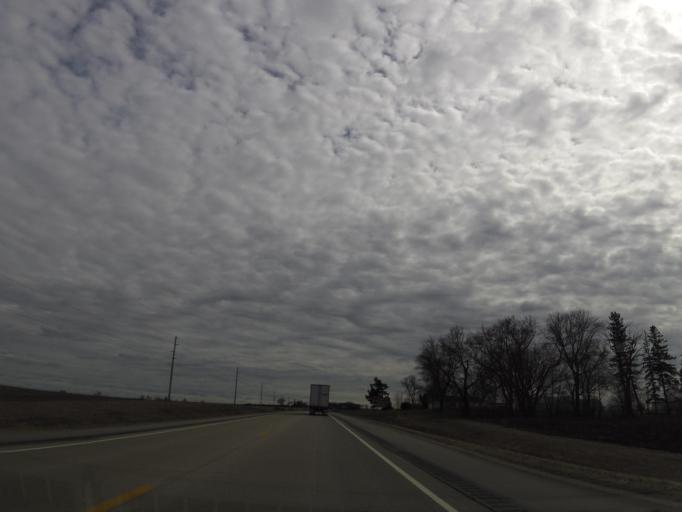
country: US
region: Minnesota
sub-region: Fillmore County
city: Spring Valley
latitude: 43.6066
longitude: -92.3894
